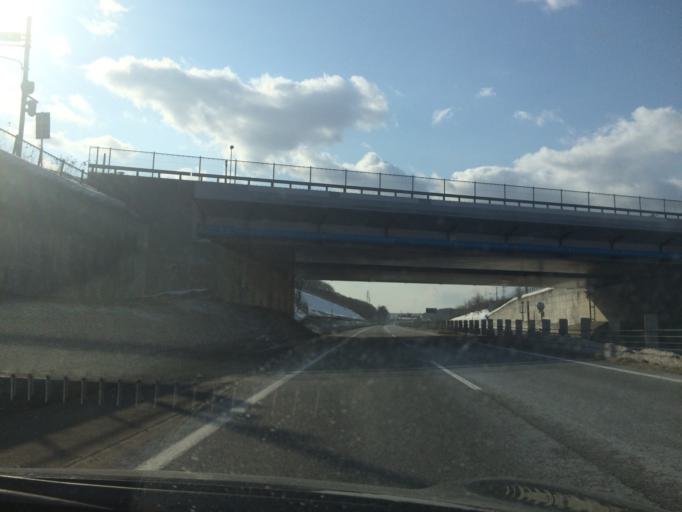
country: JP
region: Hokkaido
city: Kitahiroshima
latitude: 43.0100
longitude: 141.4661
